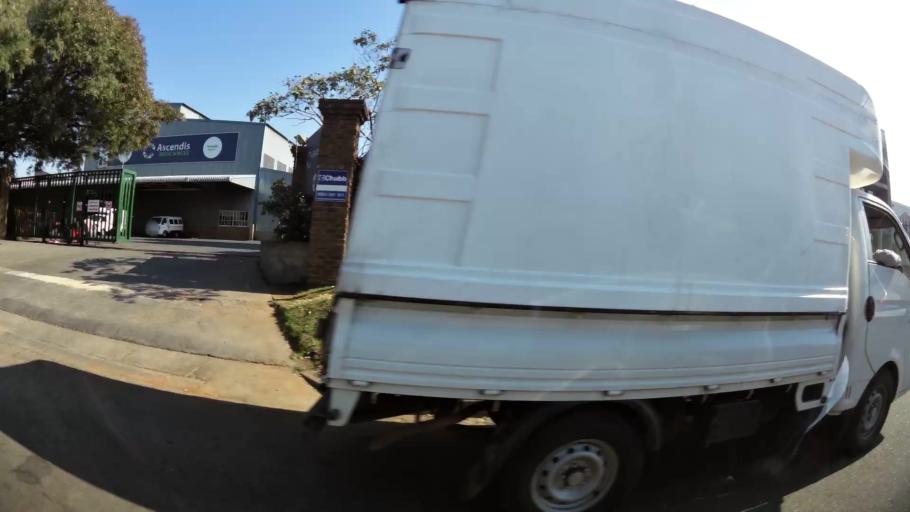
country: ZA
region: Gauteng
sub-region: City of Johannesburg Metropolitan Municipality
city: Modderfontein
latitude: -26.1445
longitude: 28.2059
